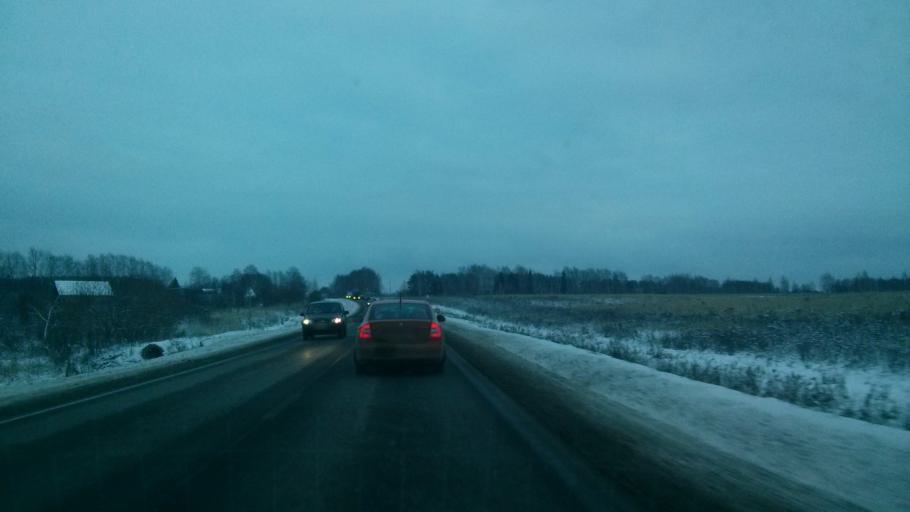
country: RU
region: Nizjnij Novgorod
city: Bogorodsk
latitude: 56.0875
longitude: 43.5202
